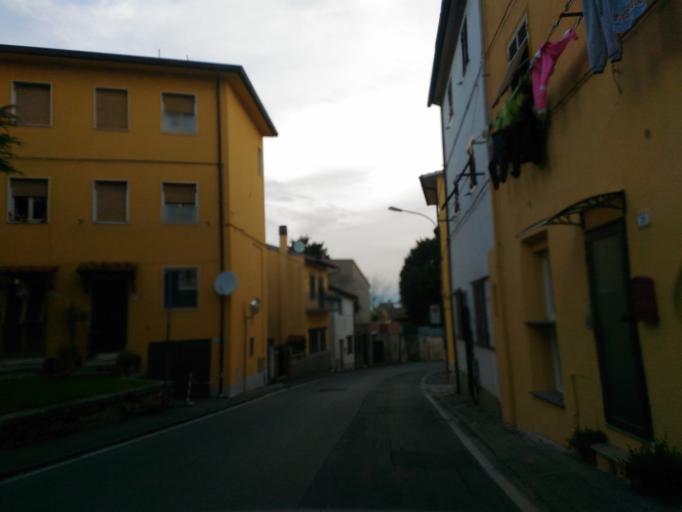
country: IT
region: Tuscany
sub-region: Provincia di Livorno
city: Collesalvetti
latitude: 43.5895
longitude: 10.4763
